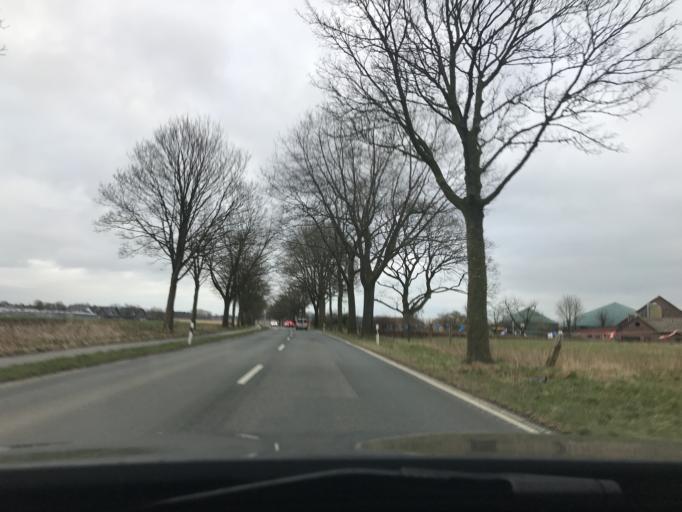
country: DE
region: North Rhine-Westphalia
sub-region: Regierungsbezirk Dusseldorf
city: Uedem
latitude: 51.6882
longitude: 6.2556
